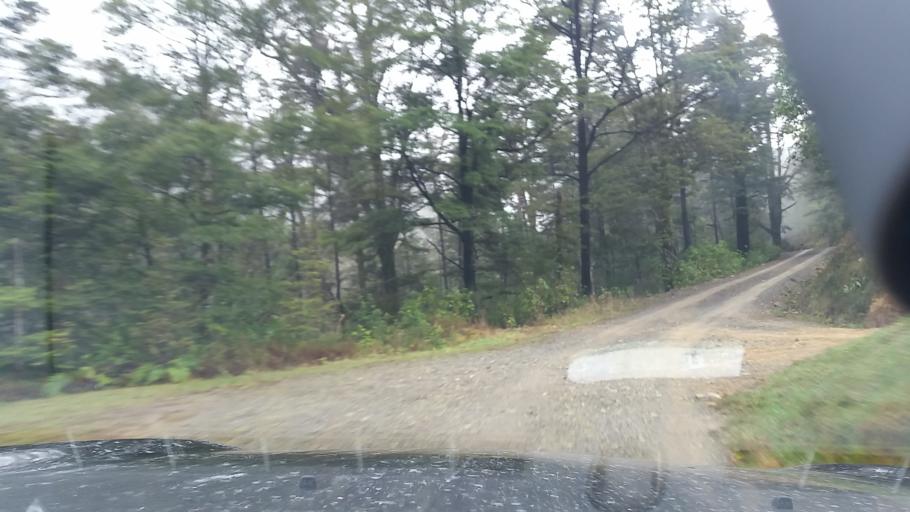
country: NZ
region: Nelson
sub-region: Nelson City
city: Nelson
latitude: -41.3755
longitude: 173.5947
